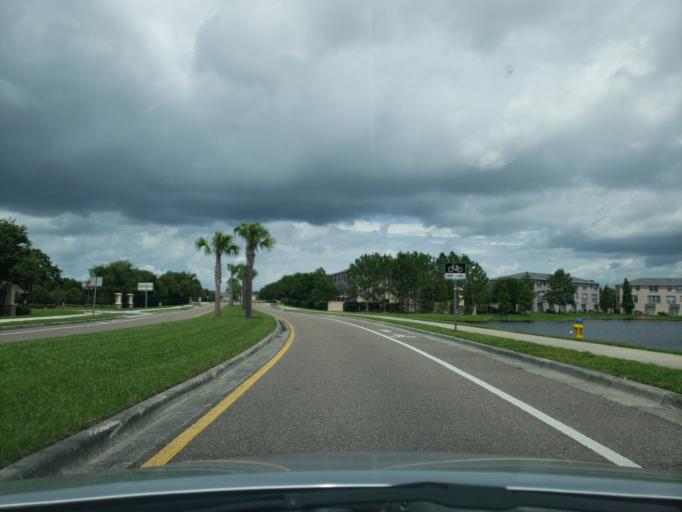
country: US
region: Florida
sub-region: Hillsborough County
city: Progress Village
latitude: 27.9139
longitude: -82.3265
